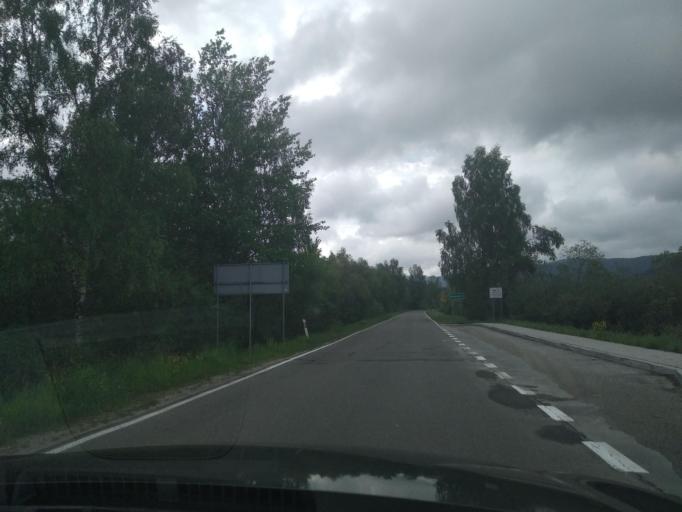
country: PL
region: Subcarpathian Voivodeship
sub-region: Powiat bieszczadzki
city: Lutowiska
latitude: 49.1044
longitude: 22.6477
